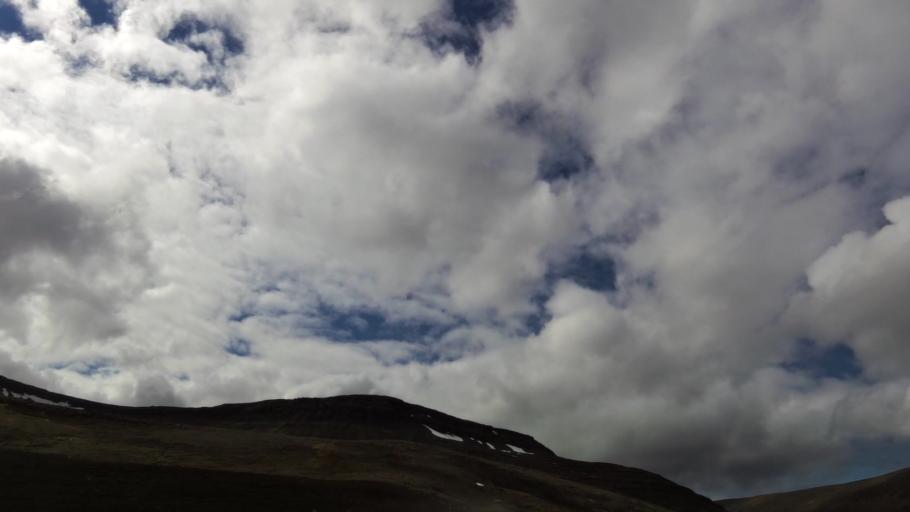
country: IS
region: Westfjords
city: Isafjoerdur
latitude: 66.1644
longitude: -23.3300
